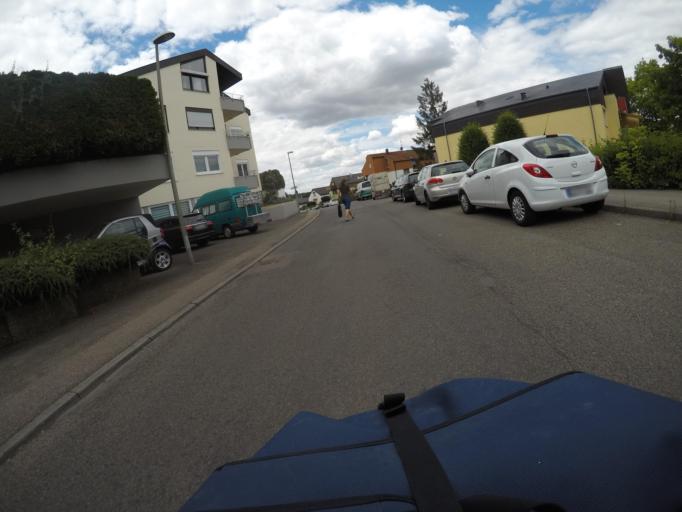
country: DE
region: Baden-Wuerttemberg
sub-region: Regierungsbezirk Stuttgart
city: Stuttgart Feuerbach
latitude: 48.8057
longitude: 9.1460
